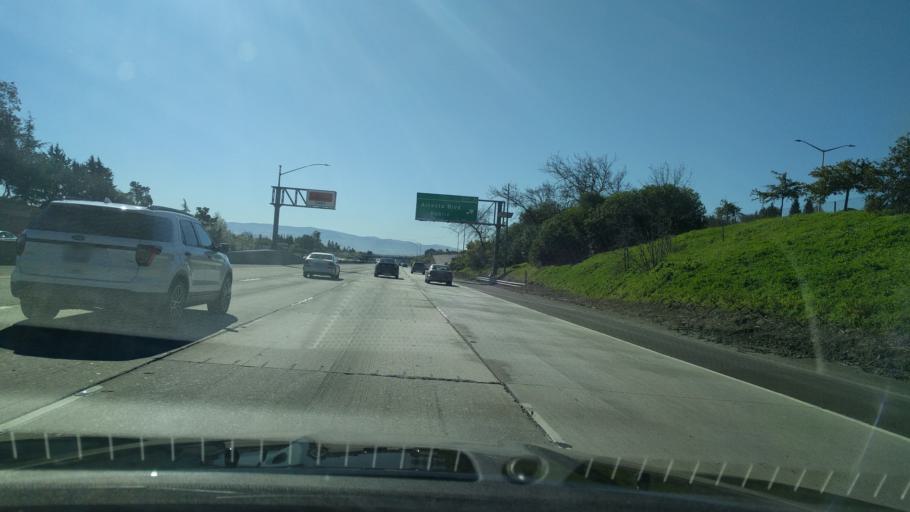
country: US
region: California
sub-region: Alameda County
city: Dublin
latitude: 37.7296
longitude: -121.9451
